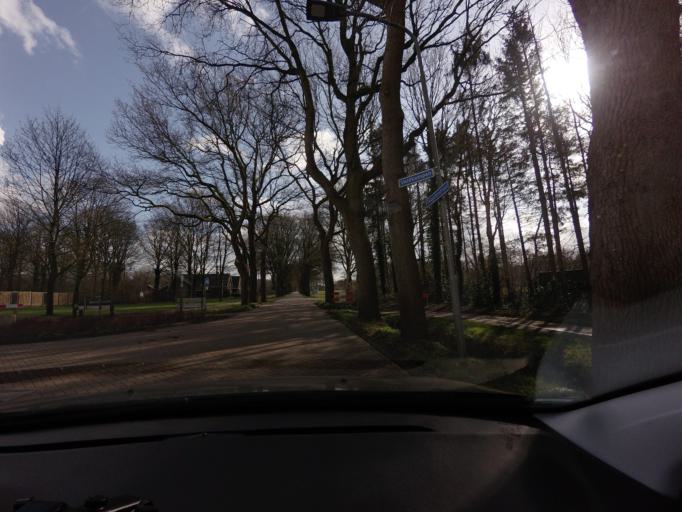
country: NL
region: Drenthe
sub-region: Gemeente Assen
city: Assen
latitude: 52.8561
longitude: 6.5954
